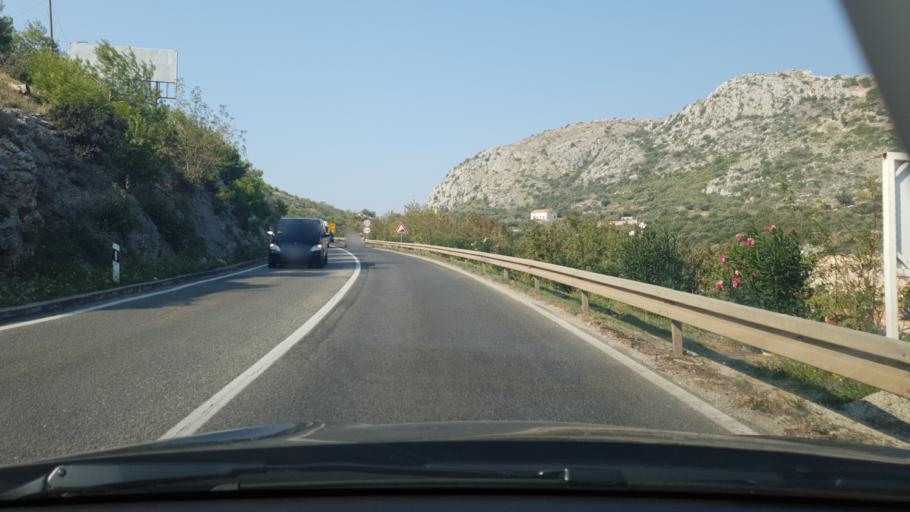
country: HR
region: Dubrovacko-Neretvanska
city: Cibaca
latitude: 42.6291
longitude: 18.1604
